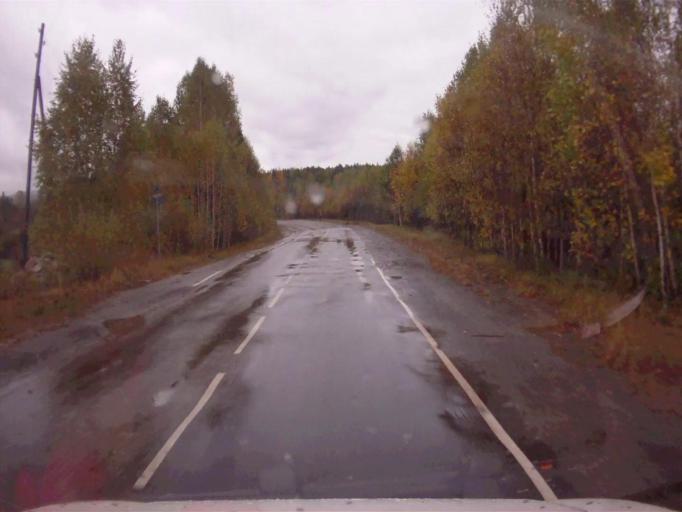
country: RU
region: Chelyabinsk
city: Kyshtym
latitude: 55.8225
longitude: 60.4768
